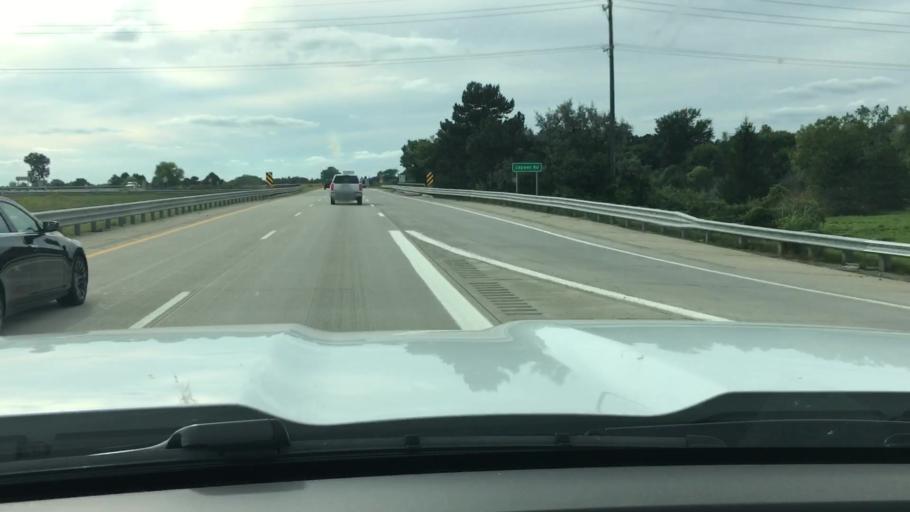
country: US
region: Michigan
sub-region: Lapeer County
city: Lapeer
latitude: 43.0247
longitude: -83.3182
